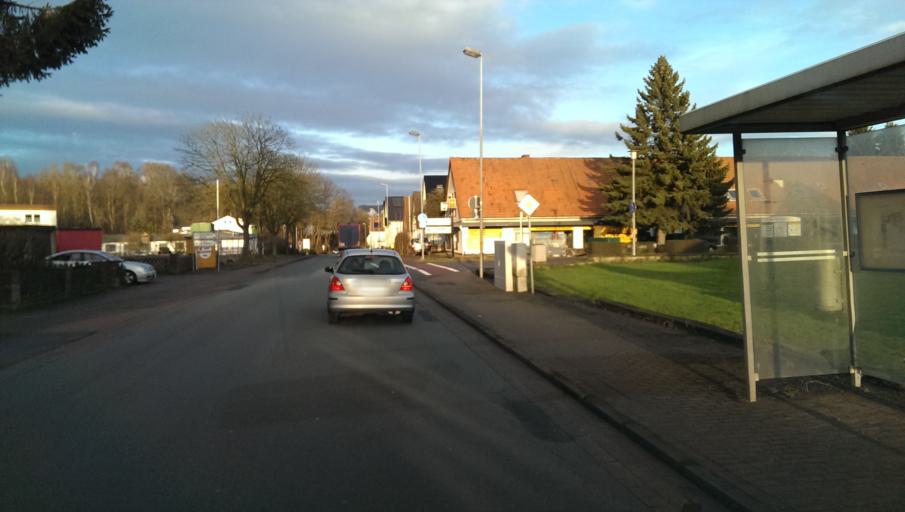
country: DE
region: Lower Saxony
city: Stadtoldendorf
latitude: 51.8808
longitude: 9.6130
